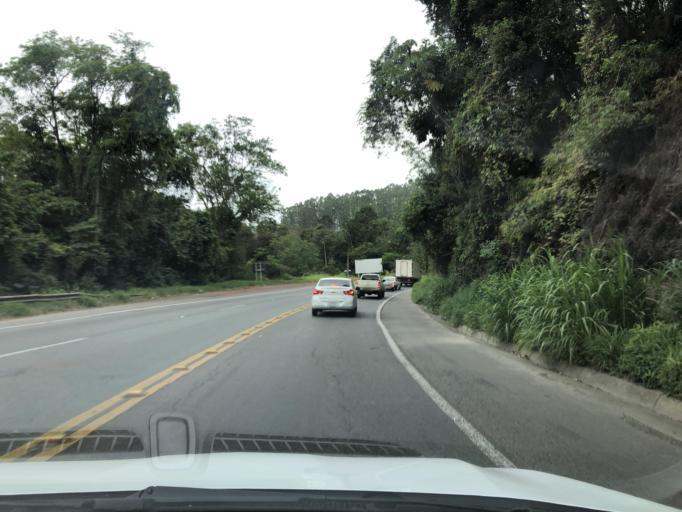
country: BR
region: Santa Catarina
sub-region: Ibirama
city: Ibirama
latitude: -27.0927
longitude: -49.5239
